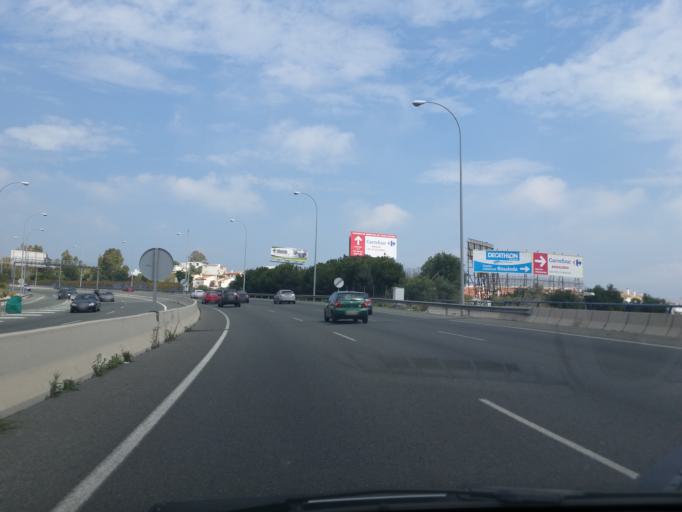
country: ES
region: Andalusia
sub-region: Provincia de Malaga
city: Malaga
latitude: 36.7255
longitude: -4.4538
